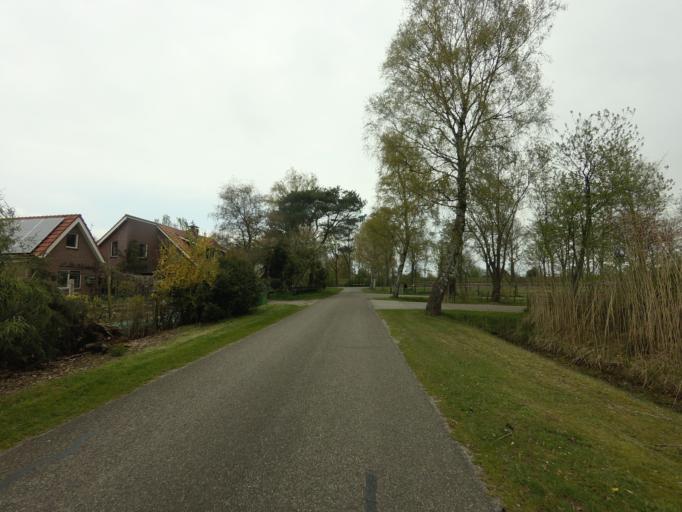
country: NL
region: Utrecht
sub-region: Gemeente Utrechtse Heuvelrug
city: Overberg
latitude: 52.0495
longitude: 5.5163
